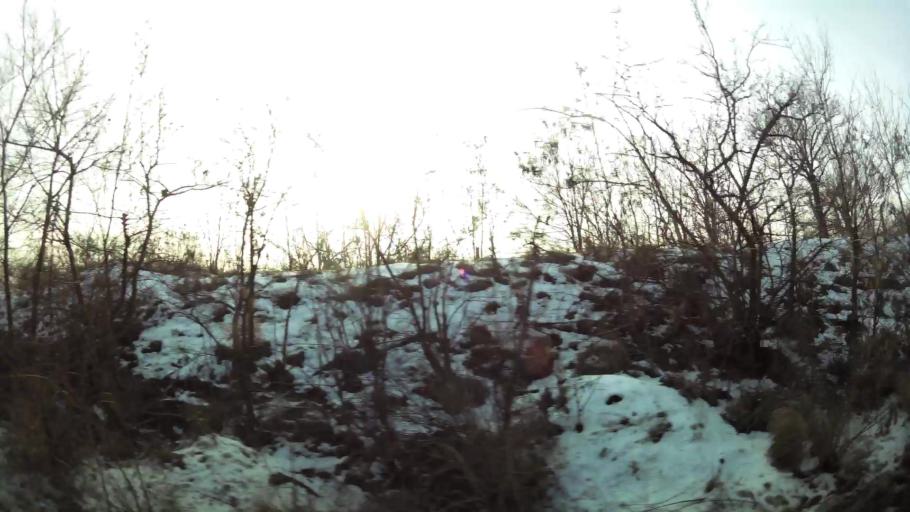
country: MK
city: Miladinovci
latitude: 41.9760
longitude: 21.6310
